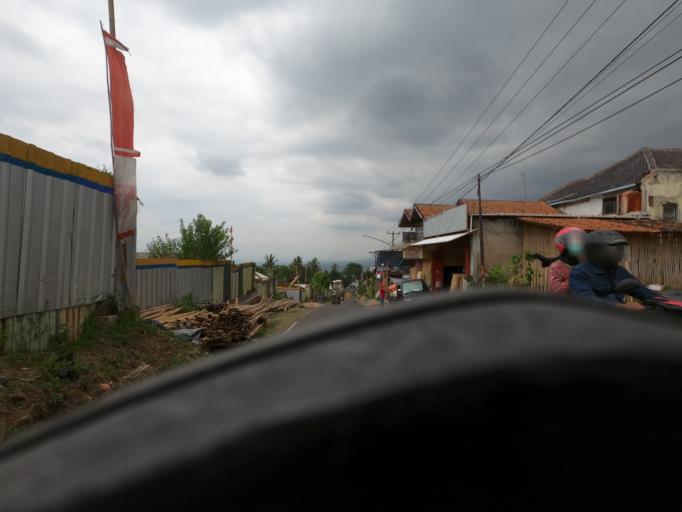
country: ID
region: West Java
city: Padalarang
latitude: -6.8353
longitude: 107.5148
